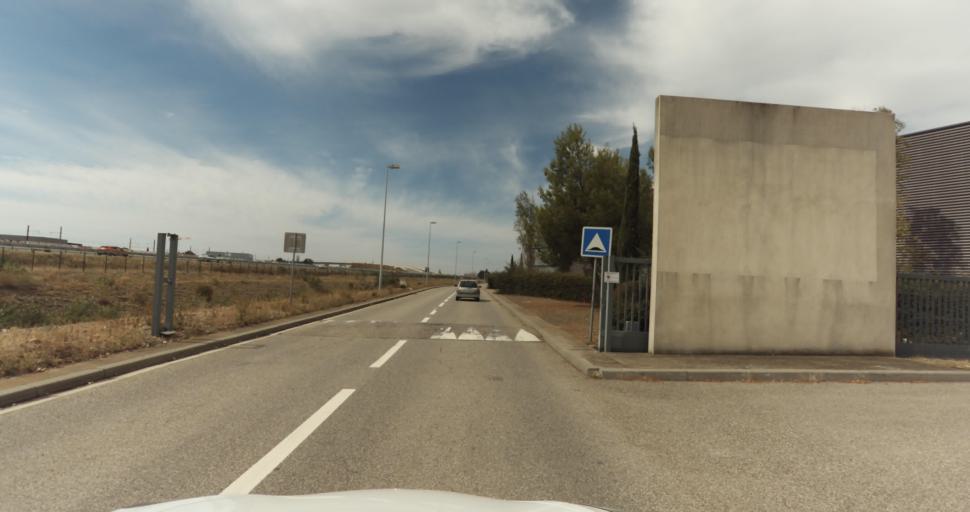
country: FR
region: Provence-Alpes-Cote d'Azur
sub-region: Departement des Bouches-du-Rhone
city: Miramas
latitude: 43.6014
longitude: 4.9975
